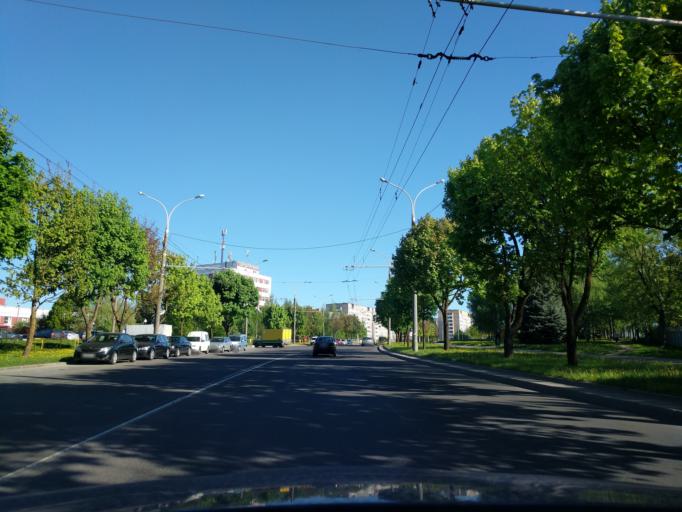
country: BY
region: Minsk
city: Novoye Medvezhino
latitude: 53.8920
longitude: 27.4531
